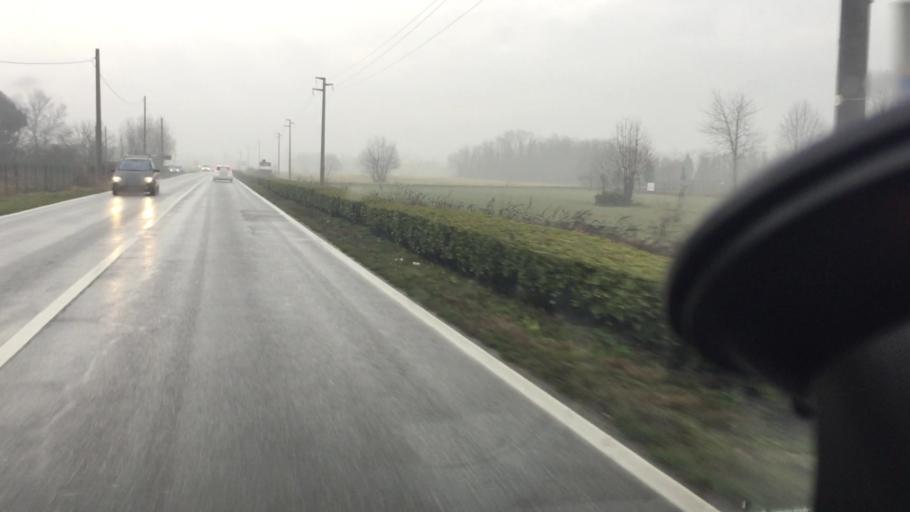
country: IT
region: Lombardy
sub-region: Citta metropolitana di Milano
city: Vaprio d'Adda
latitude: 45.5888
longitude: 9.5220
